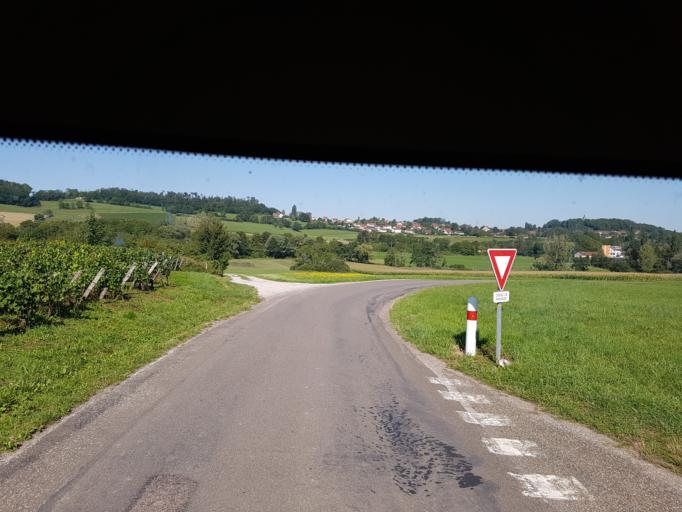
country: FR
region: Franche-Comte
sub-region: Departement du Jura
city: Perrigny
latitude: 46.7102
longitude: 5.5906
